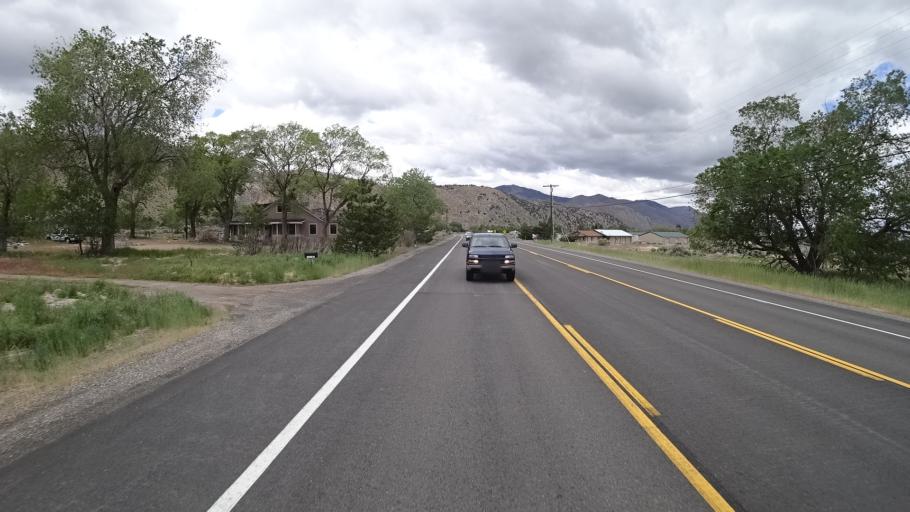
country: US
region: Nevada
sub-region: Lyon County
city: Smith Valley
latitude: 38.5145
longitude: -119.4748
